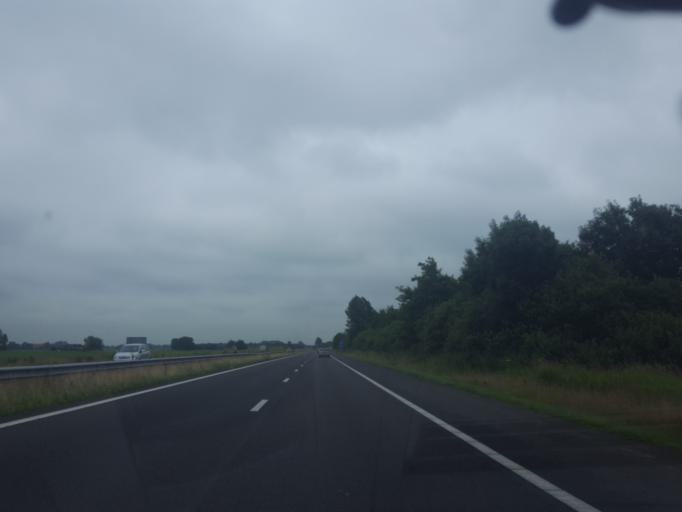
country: NL
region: Friesland
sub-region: Gemeente Boarnsterhim
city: Reduzum
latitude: 53.1221
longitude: 5.8073
